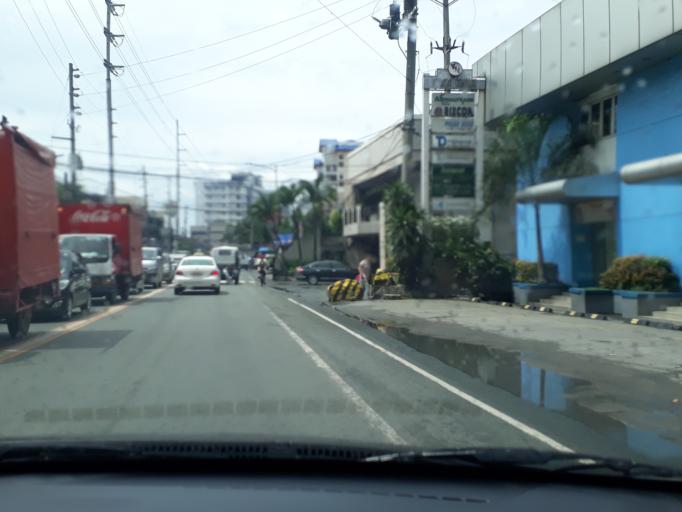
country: PH
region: Metro Manila
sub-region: Marikina
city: Calumpang
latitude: 14.6038
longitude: 121.0920
